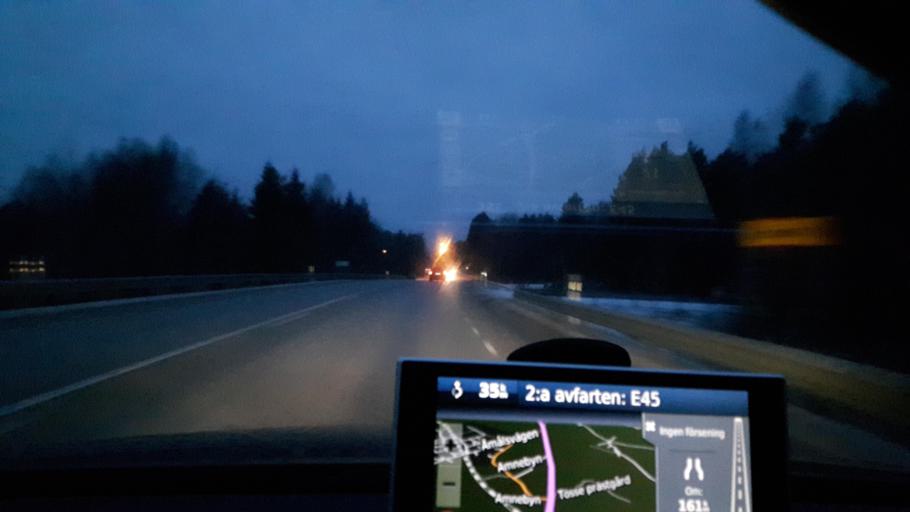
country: SE
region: Vaestra Goetaland
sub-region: Amals Kommun
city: Amal
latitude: 58.9826
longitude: 12.6528
